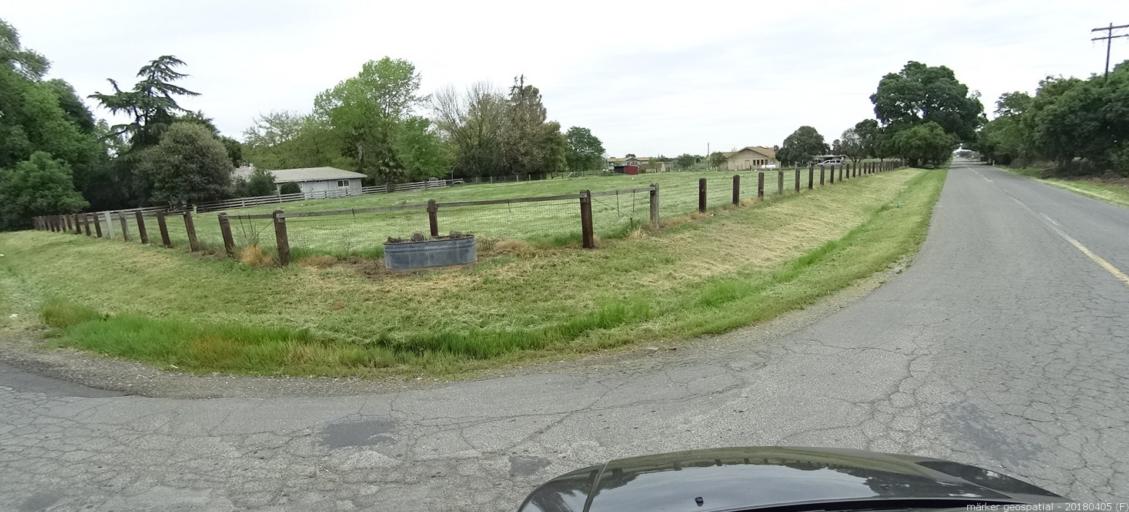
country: US
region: California
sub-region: Sacramento County
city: Galt
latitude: 38.2402
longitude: -121.3260
